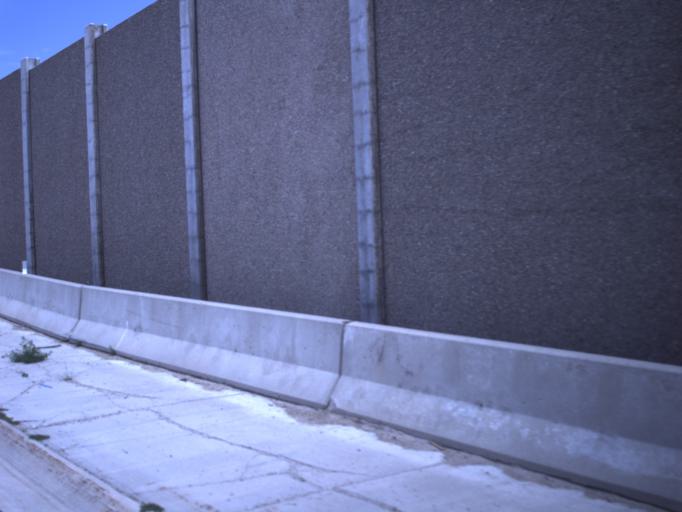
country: US
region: Utah
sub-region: Salt Lake County
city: Bluffdale
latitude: 40.4982
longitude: -111.9306
